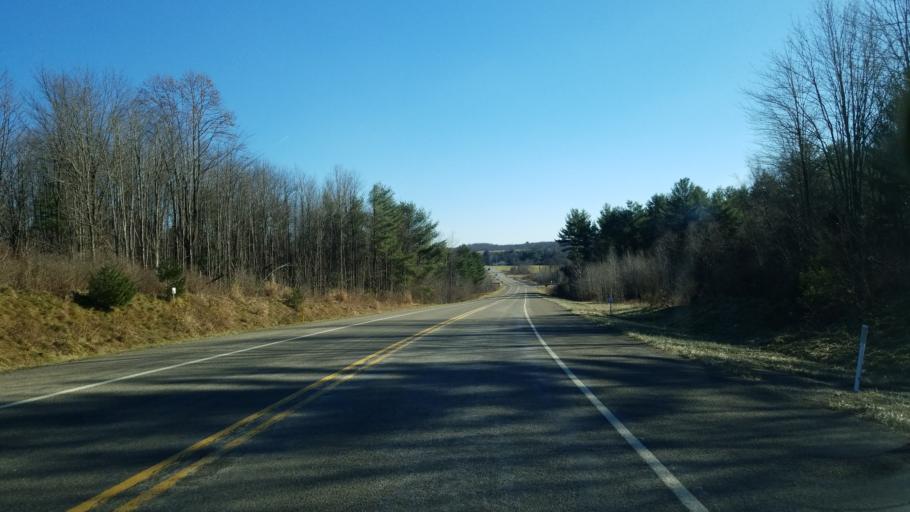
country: US
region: Pennsylvania
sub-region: Jefferson County
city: Falls Creek
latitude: 41.1875
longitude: -78.8809
